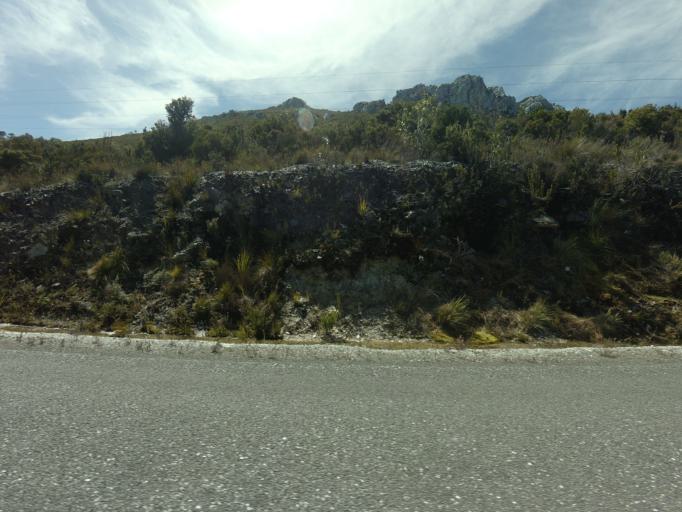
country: AU
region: Tasmania
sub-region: West Coast
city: Queenstown
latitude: -42.7961
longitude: 146.0702
